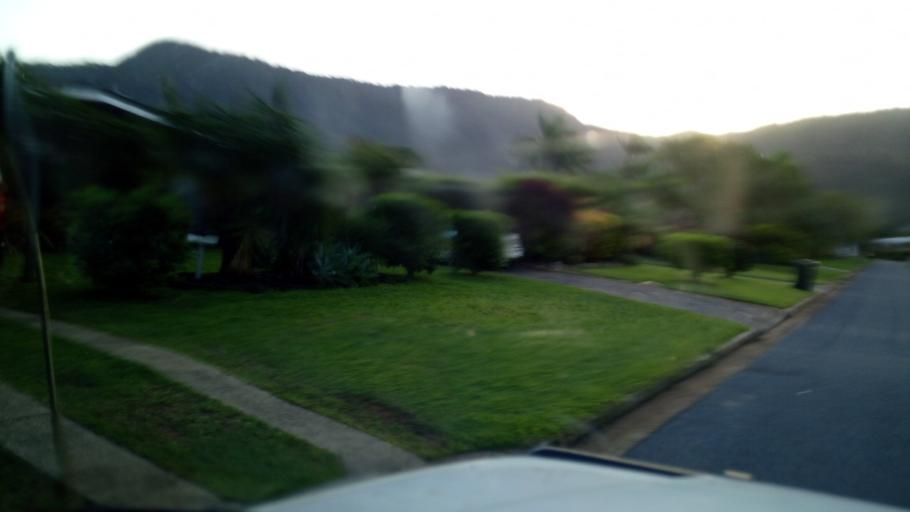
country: AU
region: Queensland
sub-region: Cairns
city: Woree
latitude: -16.9567
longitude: 145.7351
